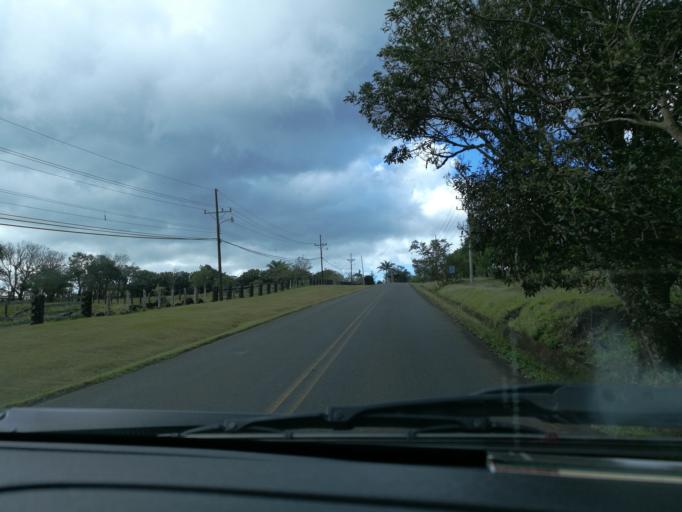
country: CR
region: Alajuela
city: Bijagua
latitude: 10.6856
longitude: -85.0872
